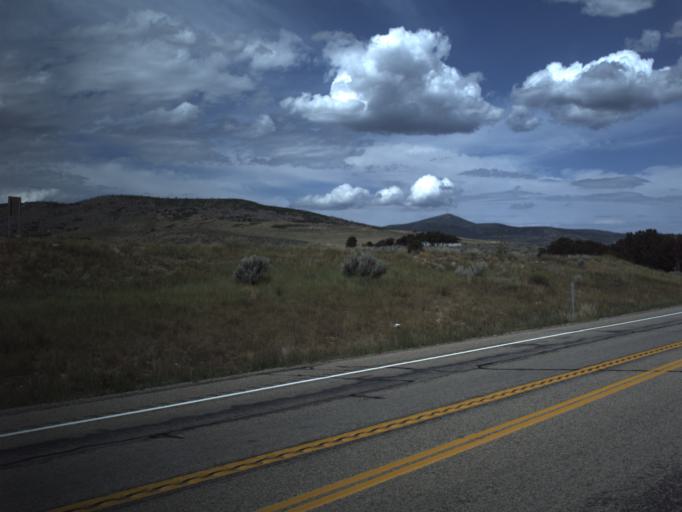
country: US
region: Utah
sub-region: Sanpete County
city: Fairview
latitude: 39.7061
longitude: -111.4693
